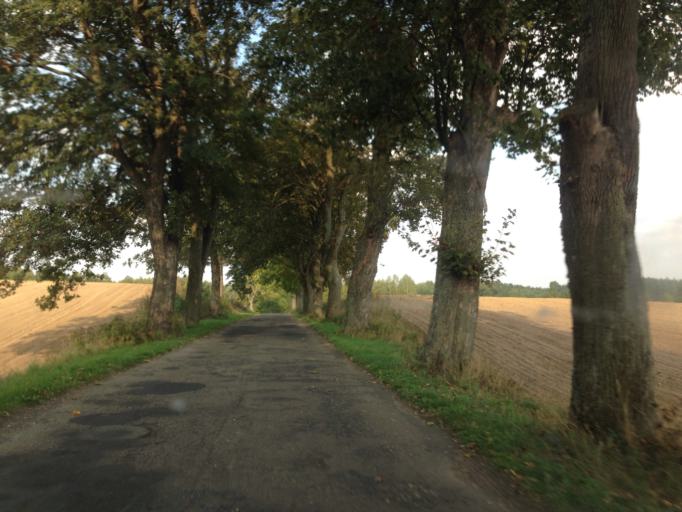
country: PL
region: Kujawsko-Pomorskie
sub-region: Powiat brodnicki
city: Gorzno
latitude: 53.2608
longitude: 19.6833
